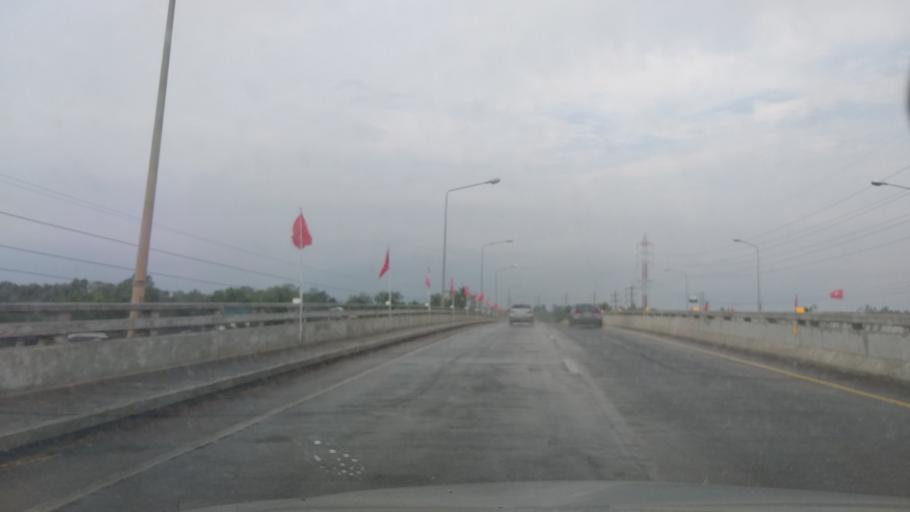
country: TH
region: Trat
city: Khao Saming
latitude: 12.3865
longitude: 102.3706
